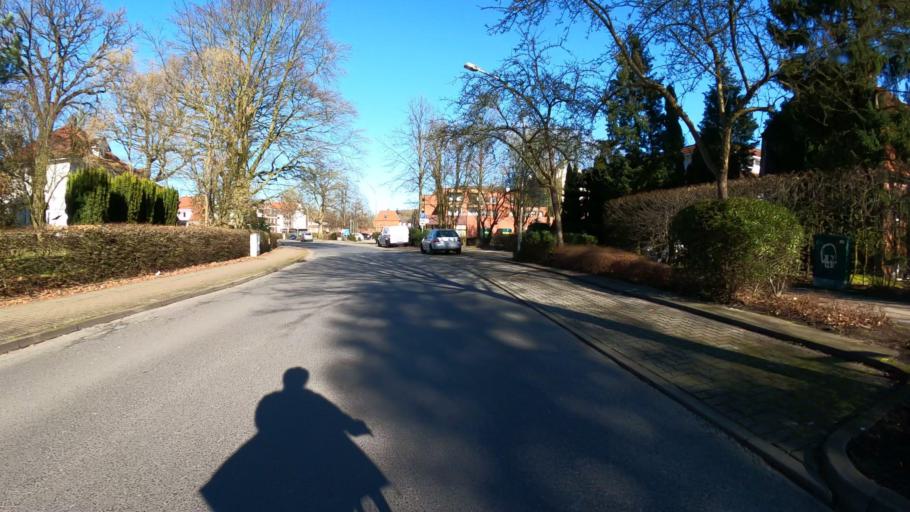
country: DE
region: Schleswig-Holstein
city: Rellingen
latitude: 53.6504
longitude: 9.7994
